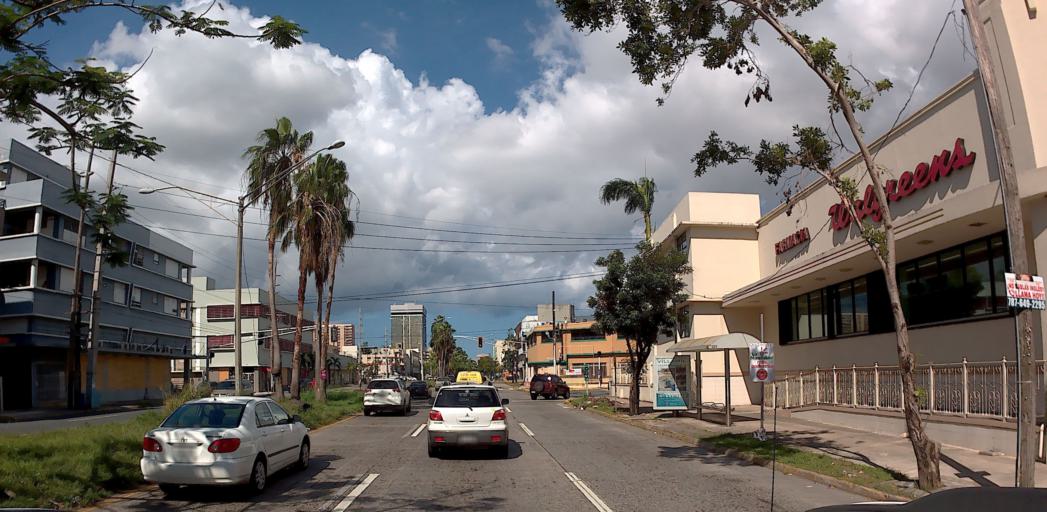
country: PR
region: Trujillo Alto
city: Trujillo Alto
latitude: 18.4028
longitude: -66.0563
